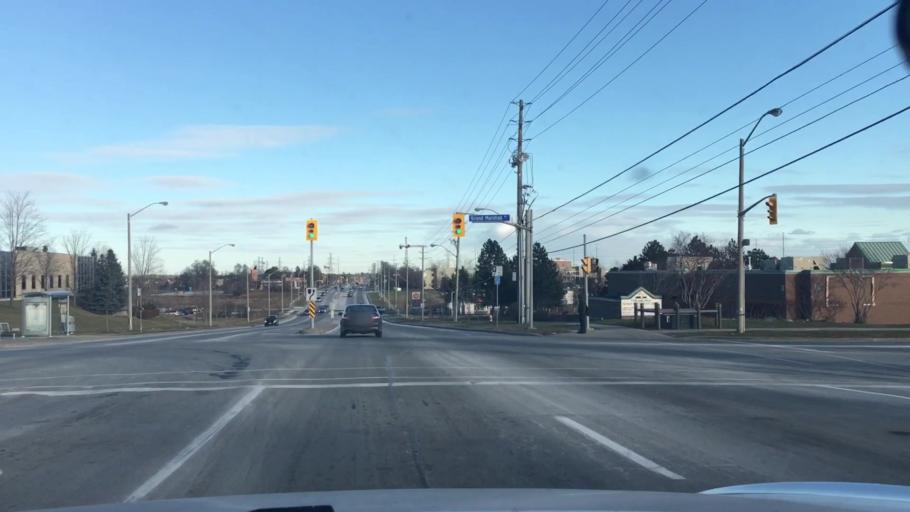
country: CA
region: Ontario
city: Scarborough
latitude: 43.8030
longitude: -79.1951
